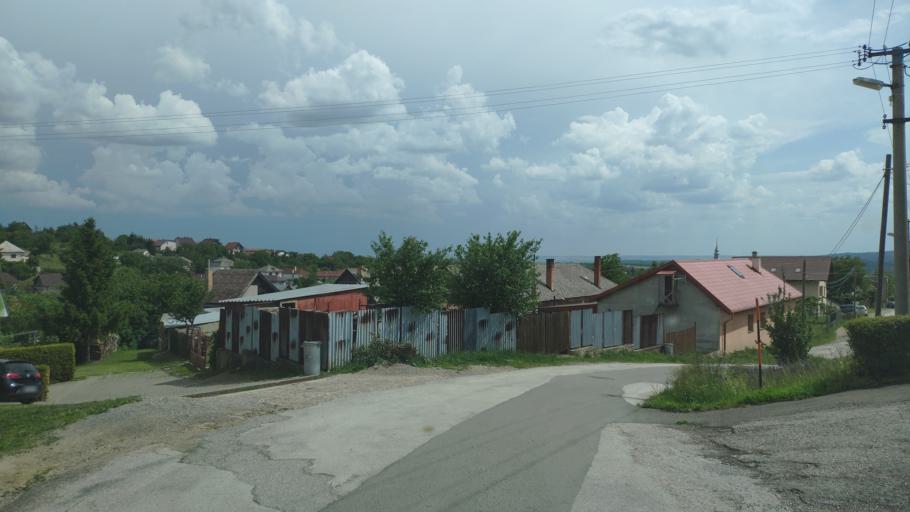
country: SK
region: Kosicky
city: Medzev
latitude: 48.7148
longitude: 20.9741
